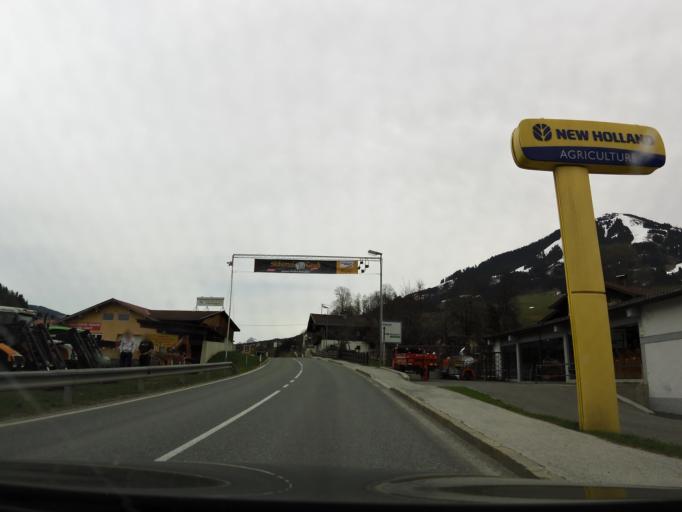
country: AT
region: Tyrol
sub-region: Politischer Bezirk Kitzbuhel
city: Westendorf
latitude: 47.4332
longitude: 12.2033
